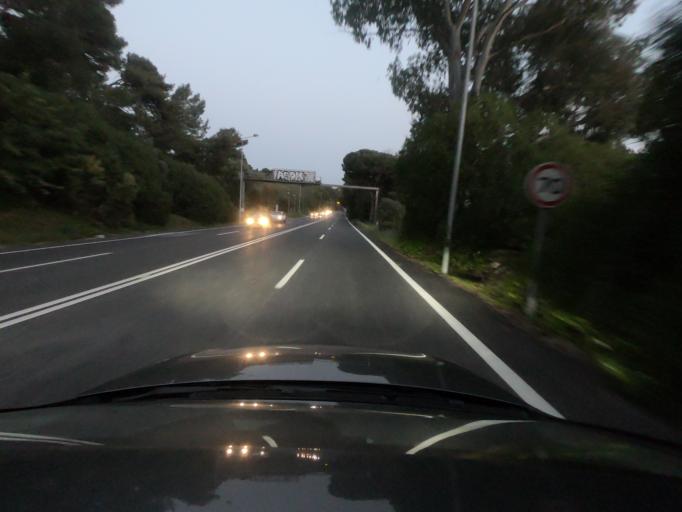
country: PT
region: Lisbon
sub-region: Oeiras
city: Quejas
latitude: 38.7063
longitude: -9.2634
